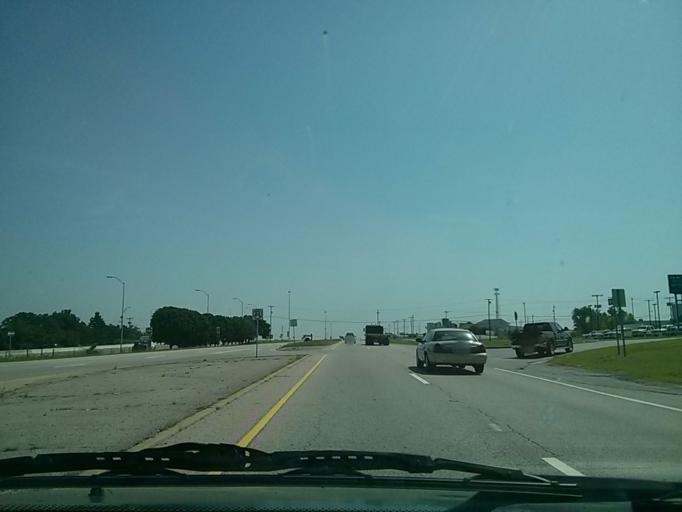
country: US
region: Oklahoma
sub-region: Tulsa County
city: Oakhurst
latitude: 36.0713
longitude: -96.0594
